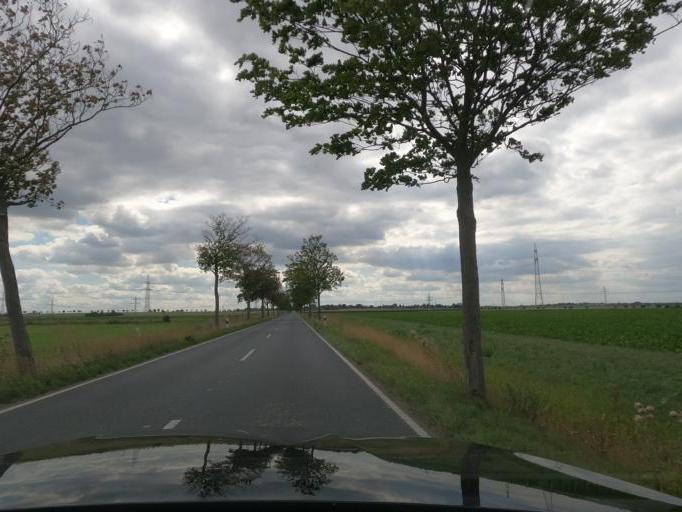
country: DE
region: Lower Saxony
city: Sehnde
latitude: 52.3327
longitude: 10.0275
